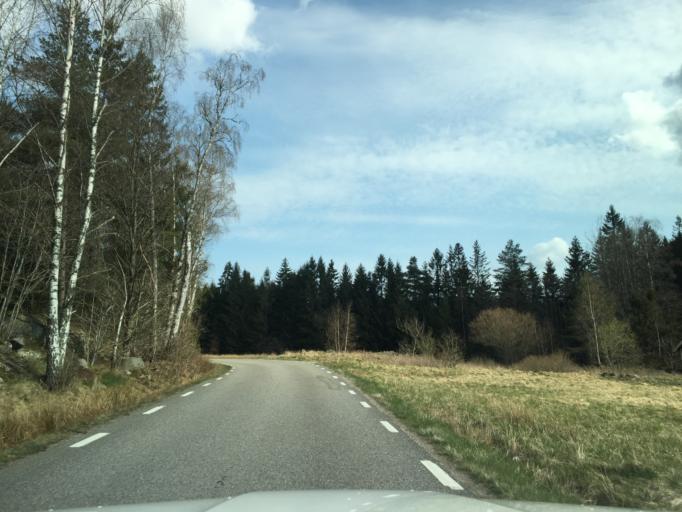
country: SE
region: Vaestra Goetaland
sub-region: Kungalvs Kommun
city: Diserod
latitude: 57.9544
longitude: 11.9558
